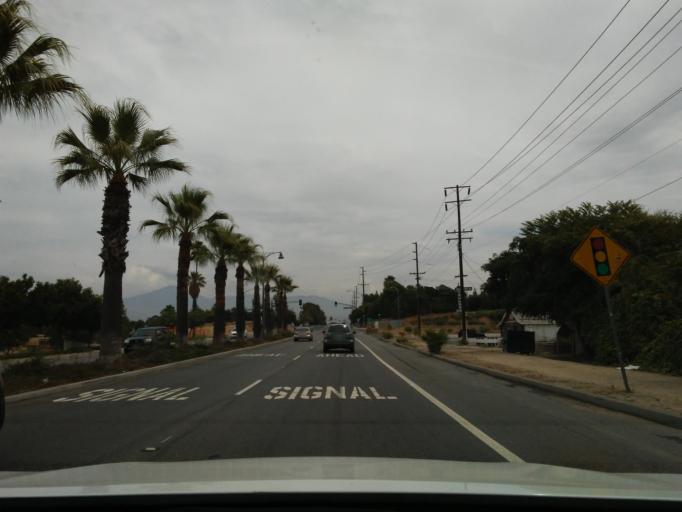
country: US
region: California
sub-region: San Bernardino County
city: Redlands
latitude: 34.0482
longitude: -117.2205
